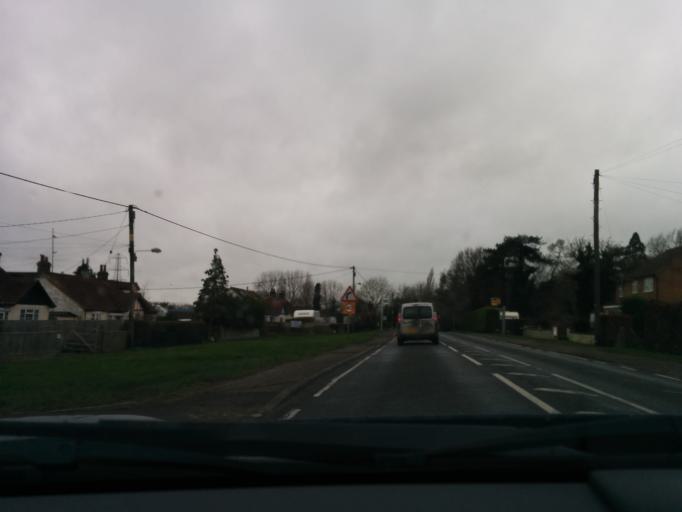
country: GB
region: England
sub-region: Oxfordshire
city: Eynsham
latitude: 51.7621
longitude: -1.3537
